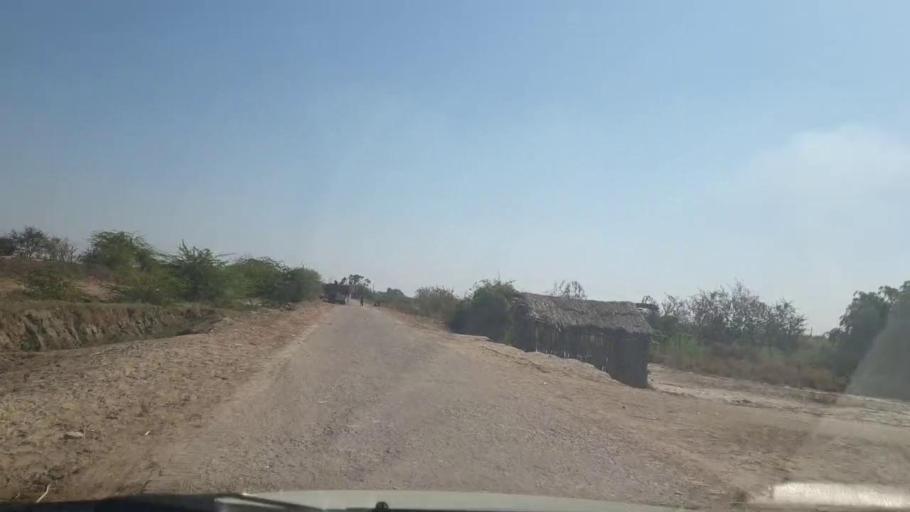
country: PK
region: Sindh
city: Mirpur Khas
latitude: 25.4858
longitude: 69.1697
